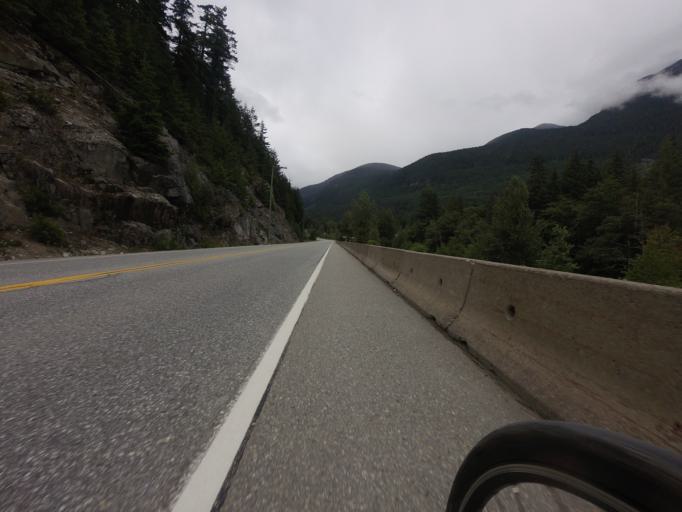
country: CA
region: British Columbia
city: Whistler
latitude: 50.1770
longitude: -122.8795
